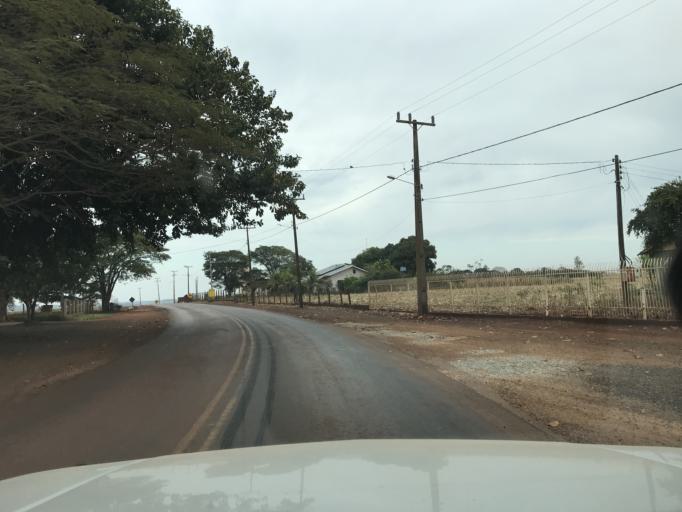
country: BR
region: Parana
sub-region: Palotina
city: Palotina
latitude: -24.4188
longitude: -53.8815
